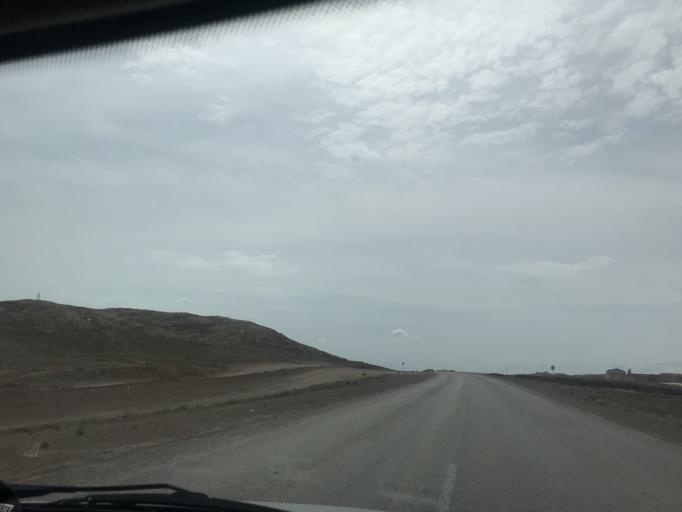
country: KZ
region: Zhambyl
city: Mynaral
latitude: 45.3709
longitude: 73.6582
